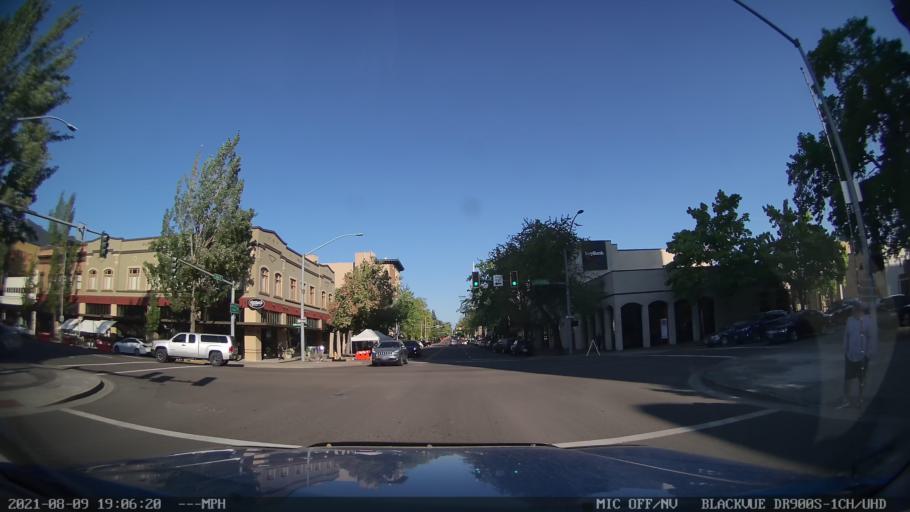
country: US
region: Oregon
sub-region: Marion County
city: Salem
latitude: 44.9400
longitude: -123.0392
